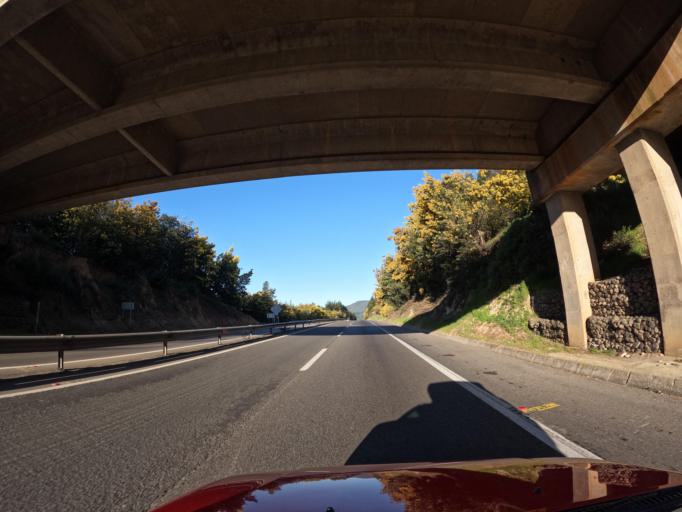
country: CL
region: Biobio
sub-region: Provincia de Nuble
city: Bulnes
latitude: -36.6948
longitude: -72.5995
